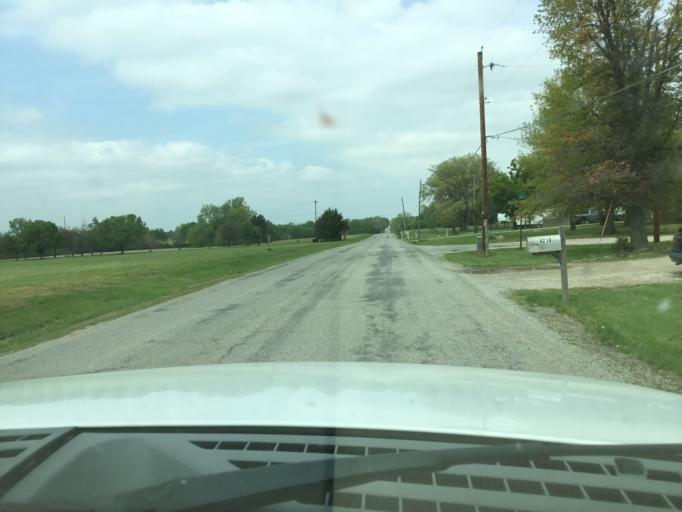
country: US
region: Kansas
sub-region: Shawnee County
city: Topeka
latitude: 38.9920
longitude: -95.5864
